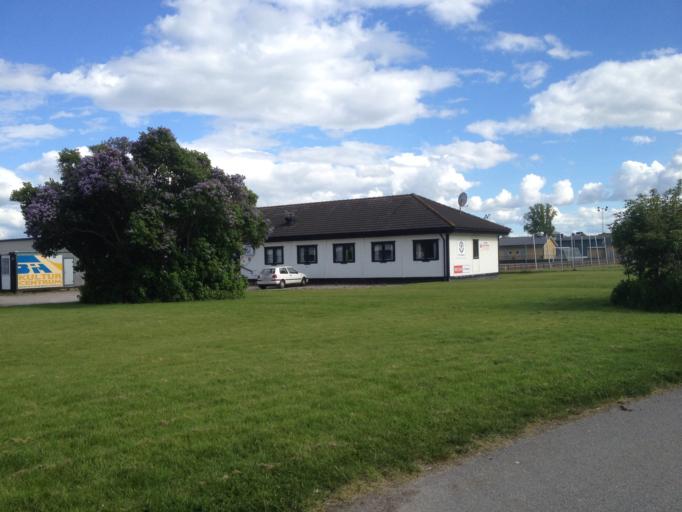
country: SE
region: OEstergoetland
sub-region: Norrkopings Kommun
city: Norrkoping
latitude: 58.6021
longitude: 16.1758
